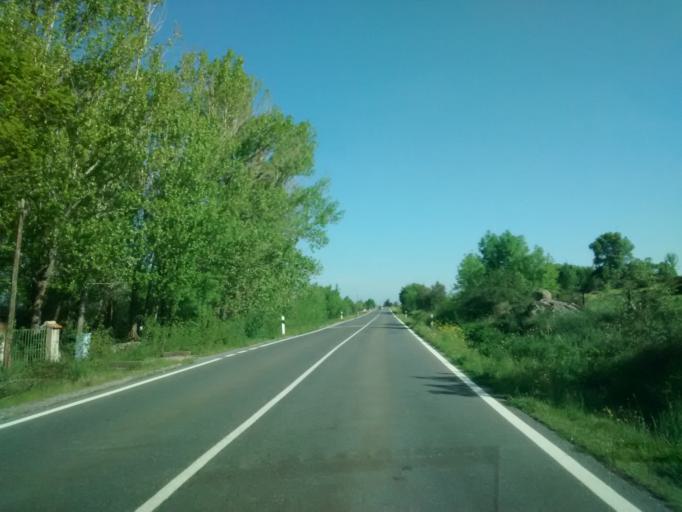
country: ES
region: Castille and Leon
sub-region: Provincia de Segovia
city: Palazuelos de Eresma
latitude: 40.9298
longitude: -4.0317
